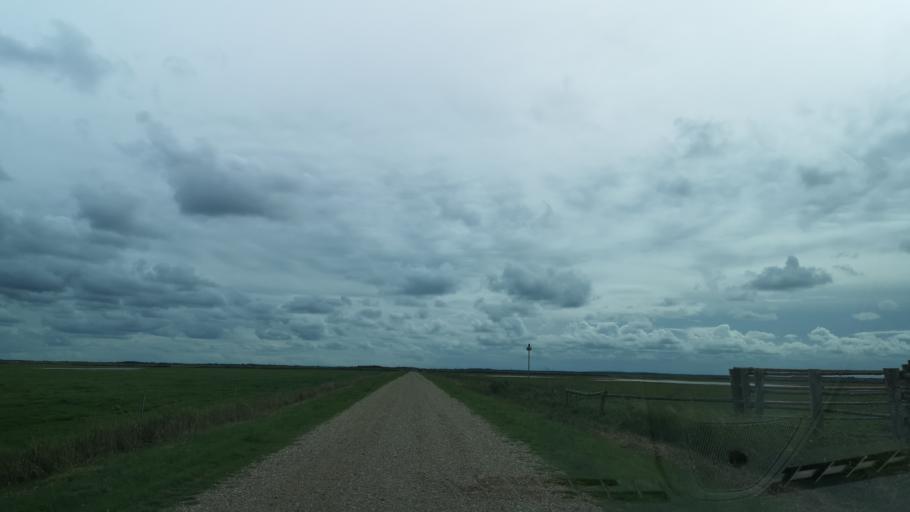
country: DK
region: Central Jutland
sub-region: Ringkobing-Skjern Kommune
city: Hvide Sande
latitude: 55.8770
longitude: 8.2252
